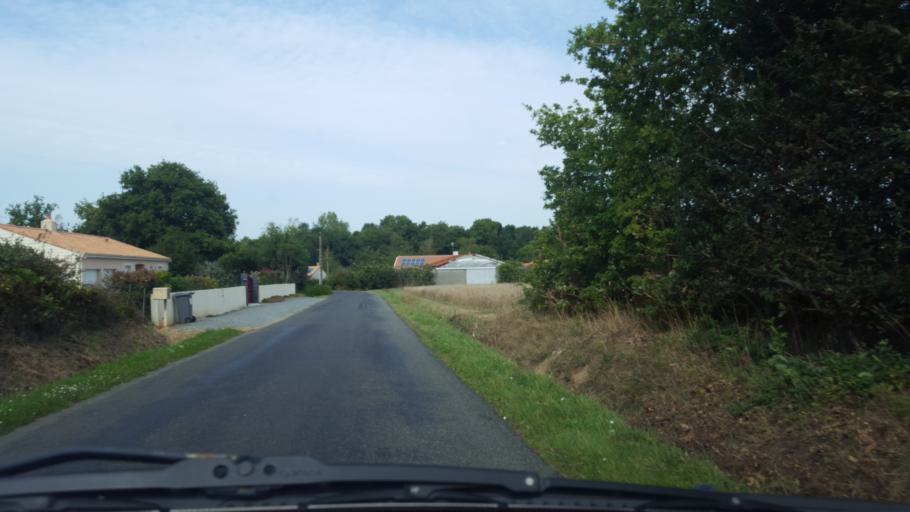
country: FR
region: Pays de la Loire
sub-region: Departement de la Loire-Atlantique
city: La Limouziniere
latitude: 46.9997
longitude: -1.6321
